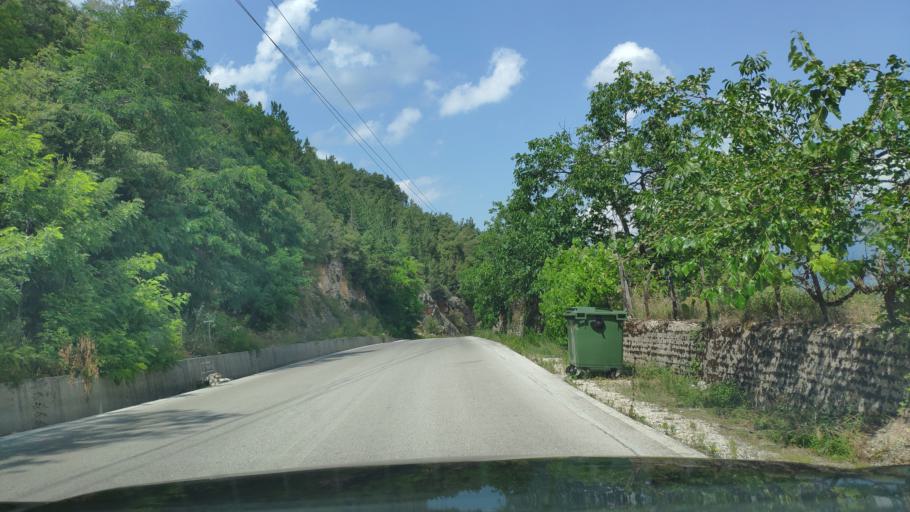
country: GR
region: Epirus
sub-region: Nomos Artas
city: Agios Dimitrios
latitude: 39.3244
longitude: 20.9951
